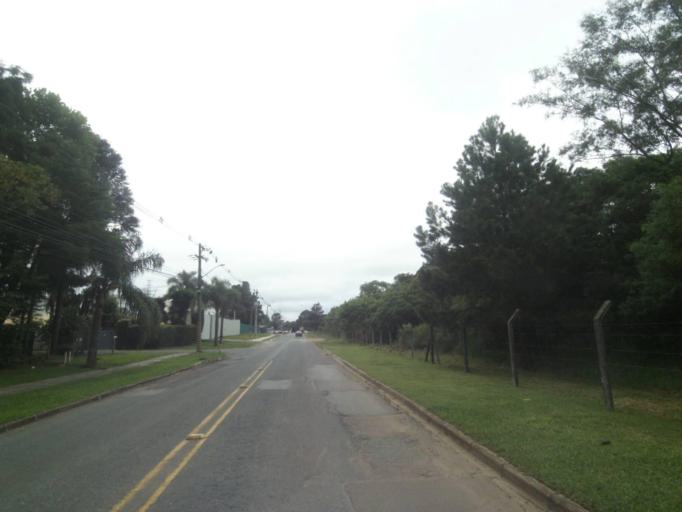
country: BR
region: Parana
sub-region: Araucaria
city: Araucaria
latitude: -25.5384
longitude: -49.3275
